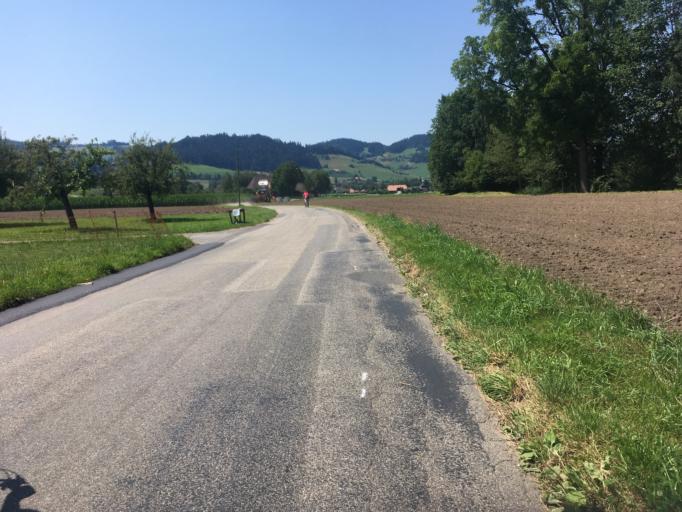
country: CH
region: Bern
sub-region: Emmental District
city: Langnau
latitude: 46.9446
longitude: 7.7637
